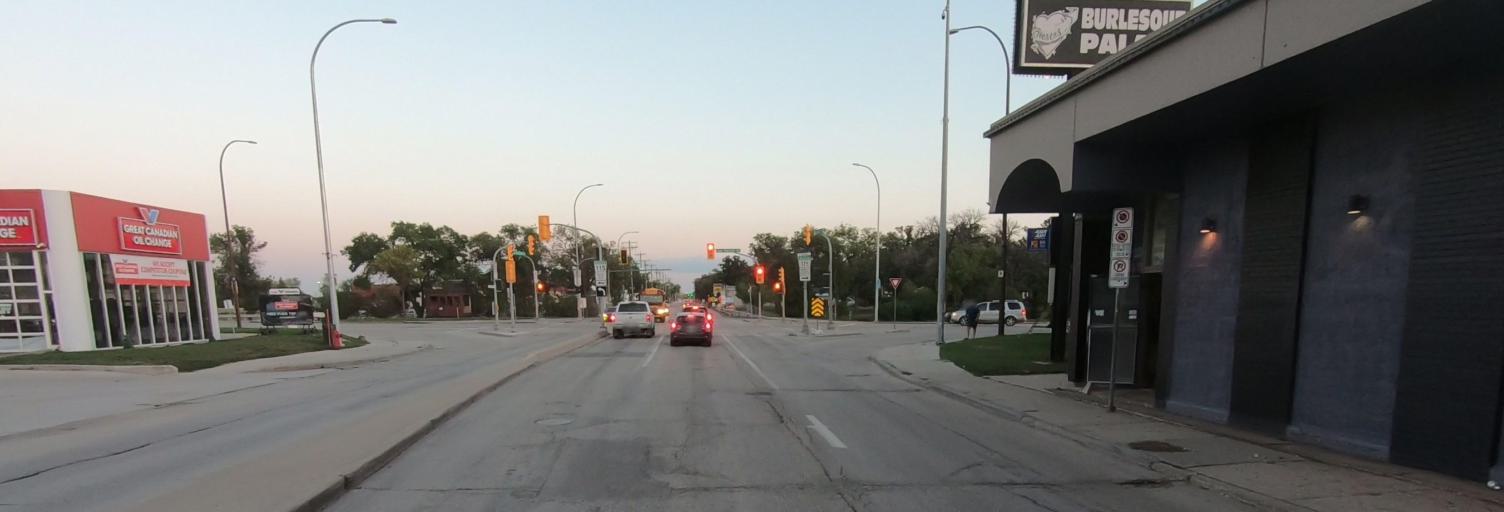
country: CA
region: Manitoba
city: Winnipeg
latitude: 49.8825
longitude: -97.0991
